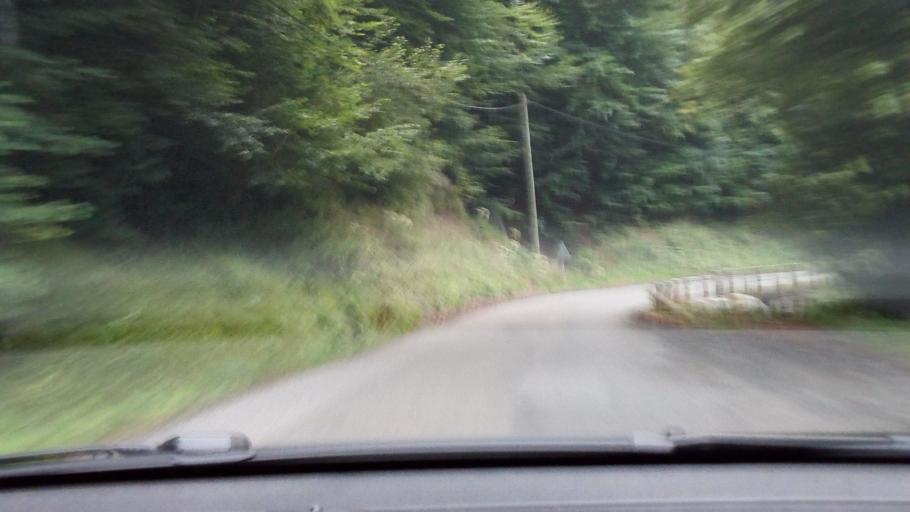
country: FR
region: Midi-Pyrenees
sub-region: Departement des Hautes-Pyrenees
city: Cauterets
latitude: 42.9513
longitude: -0.2035
